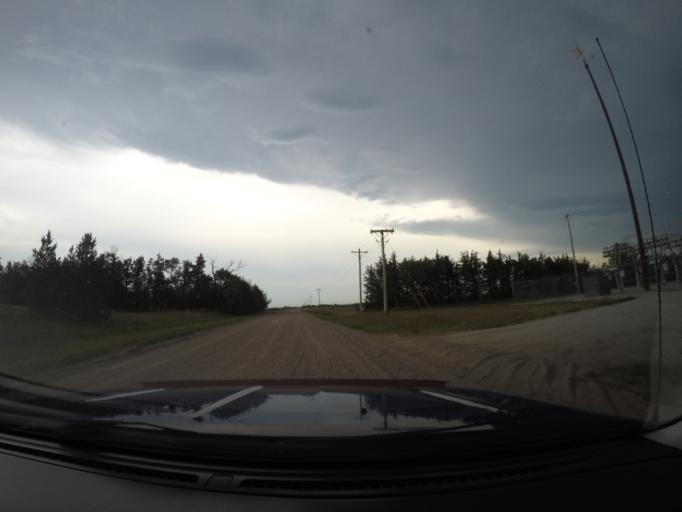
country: US
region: Nebraska
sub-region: Buffalo County
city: Kearney
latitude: 40.8439
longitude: -99.2549
